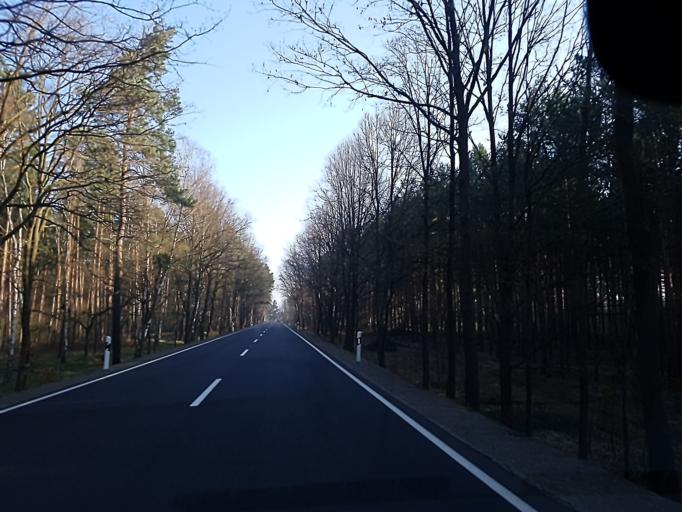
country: DE
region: Brandenburg
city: Bronkow
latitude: 51.6949
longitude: 13.9184
